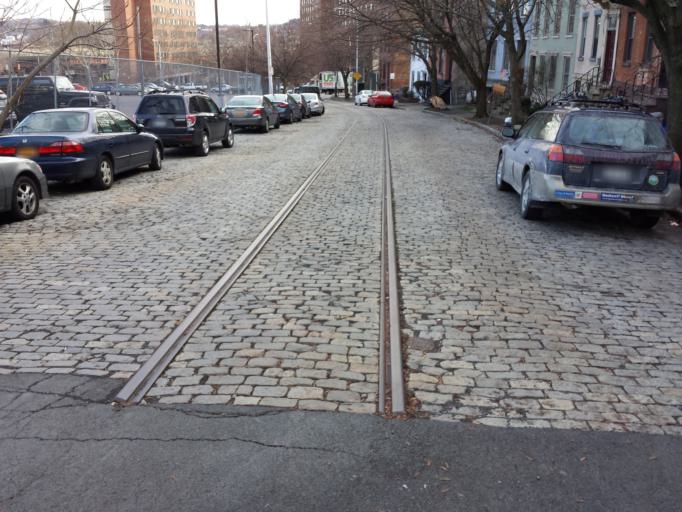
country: US
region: New York
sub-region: Albany County
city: Albany
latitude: 42.6476
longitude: -73.7571
